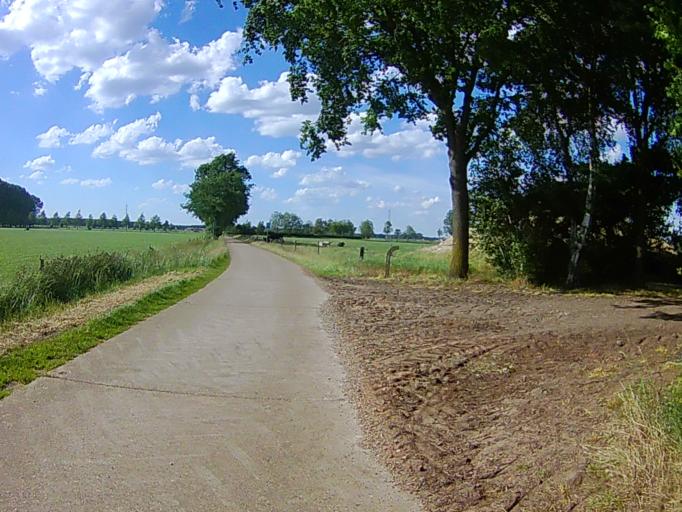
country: BE
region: Flanders
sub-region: Provincie Antwerpen
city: Lille
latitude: 51.2275
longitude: 4.8775
